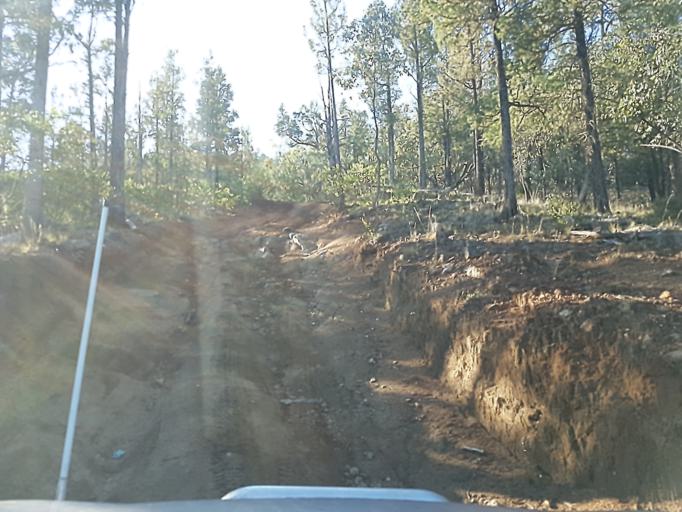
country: AU
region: New South Wales
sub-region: Snowy River
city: Jindabyne
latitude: -36.9519
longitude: 148.3800
